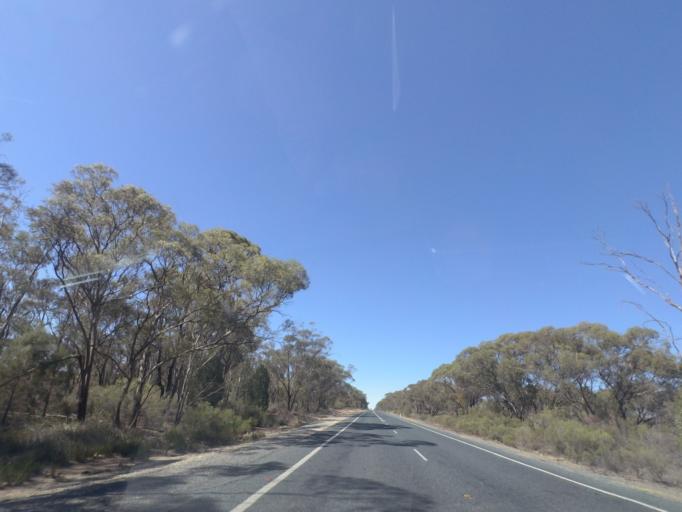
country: AU
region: New South Wales
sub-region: Bland
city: West Wyalong
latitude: -34.1225
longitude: 147.1267
